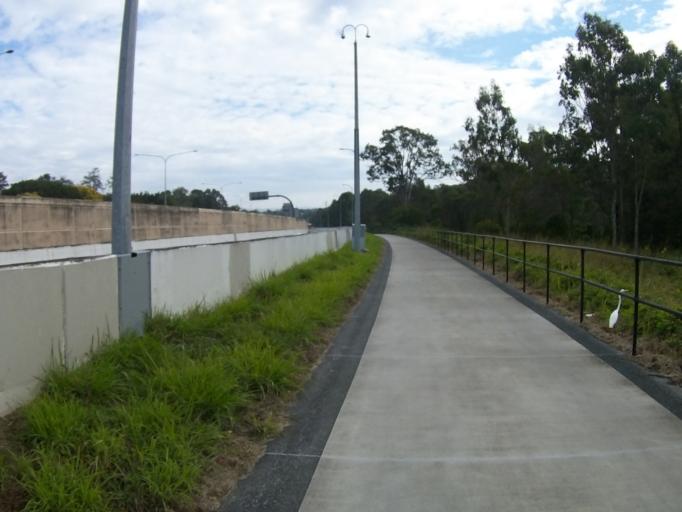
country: AU
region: Queensland
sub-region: Brisbane
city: Greenslopes
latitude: -27.5175
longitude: 153.0498
